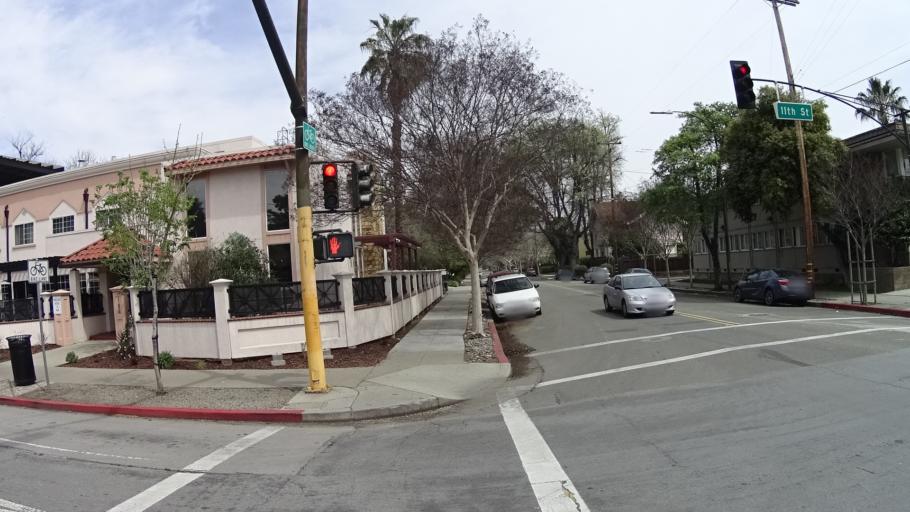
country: US
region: California
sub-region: Santa Clara County
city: San Jose
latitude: 37.3379
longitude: -121.8776
